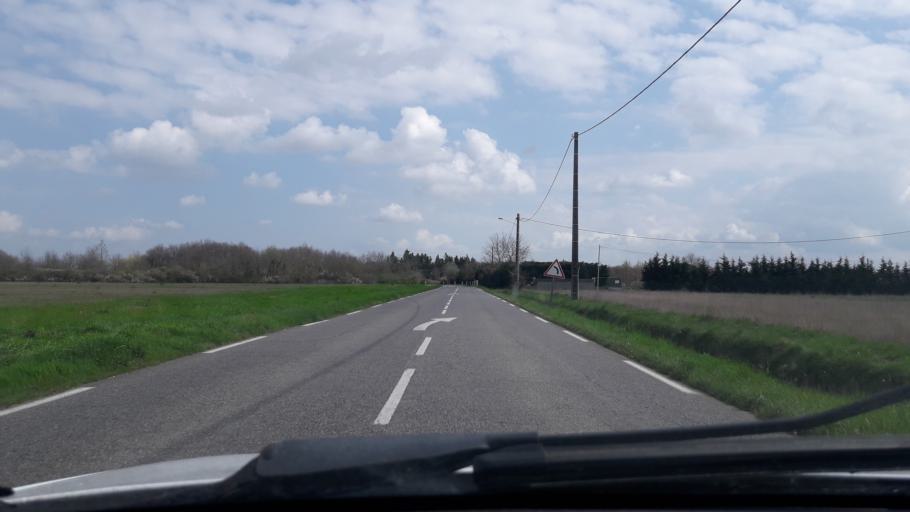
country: FR
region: Midi-Pyrenees
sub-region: Departement de la Haute-Garonne
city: Seysses
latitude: 43.5024
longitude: 1.2672
